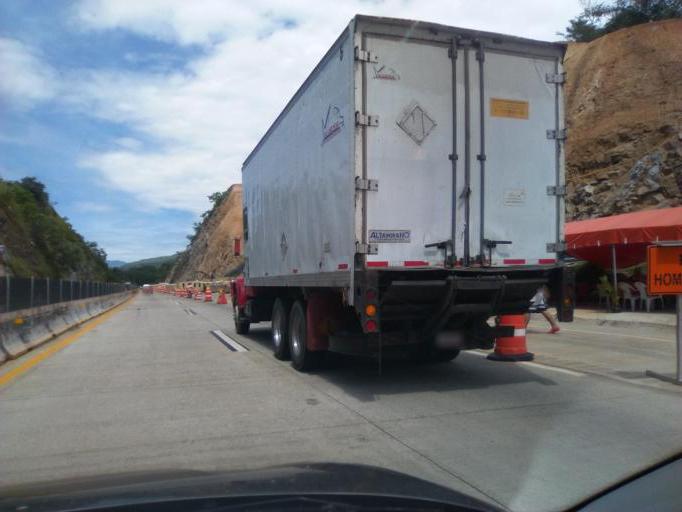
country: MX
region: Guerrero
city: Tierra Colorada
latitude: 17.1773
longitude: -99.5527
